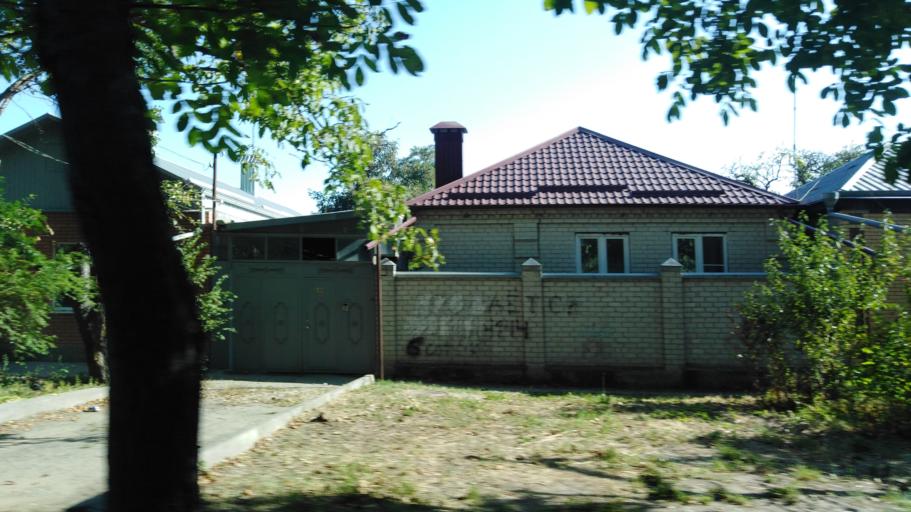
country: RU
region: Stavropol'skiy
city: Svobody
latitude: 44.0384
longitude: 43.0475
